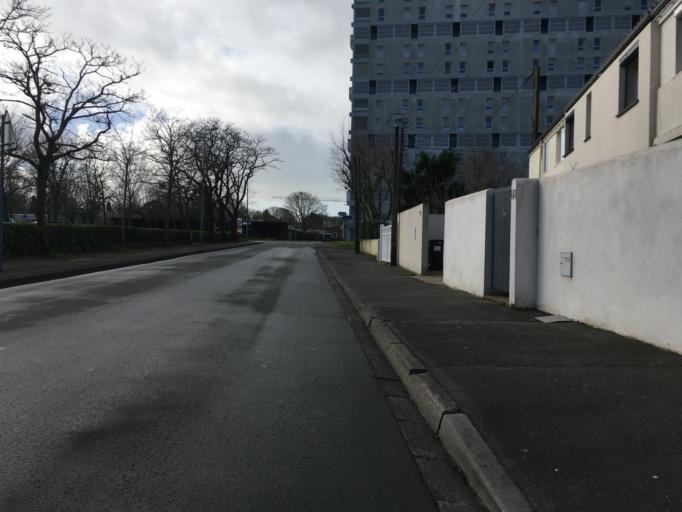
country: FR
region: Poitou-Charentes
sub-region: Departement de la Charente-Maritime
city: La Rochelle
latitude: 46.1690
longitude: -1.1870
